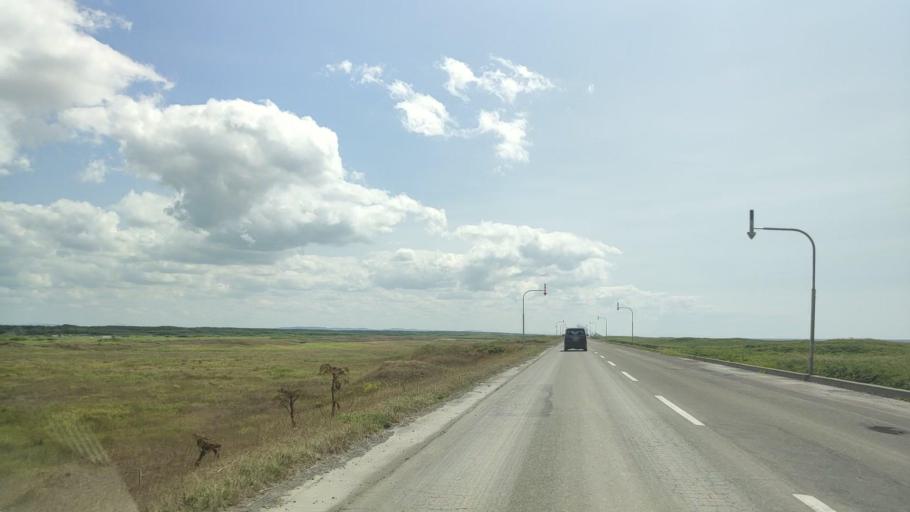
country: JP
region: Hokkaido
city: Makubetsu
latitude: 45.0234
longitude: 141.6695
